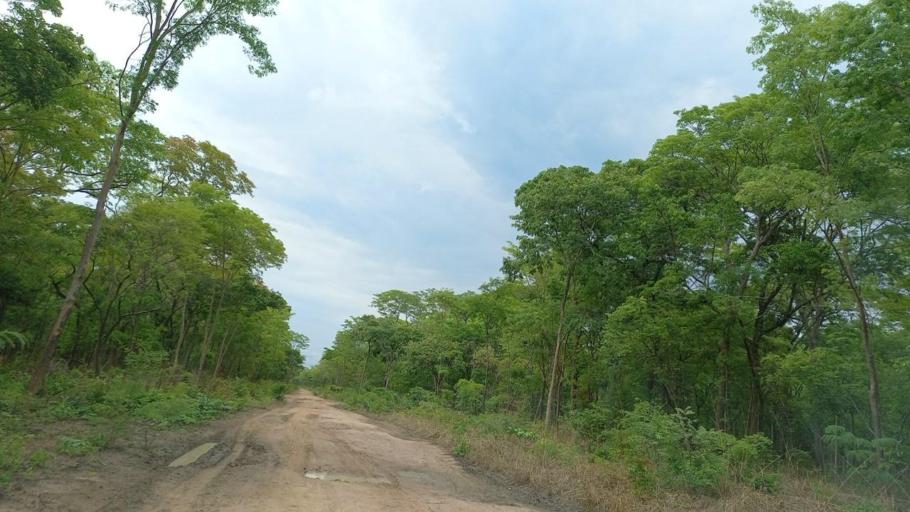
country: ZM
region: North-Western
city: Kalengwa
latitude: -13.5596
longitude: 24.9731
